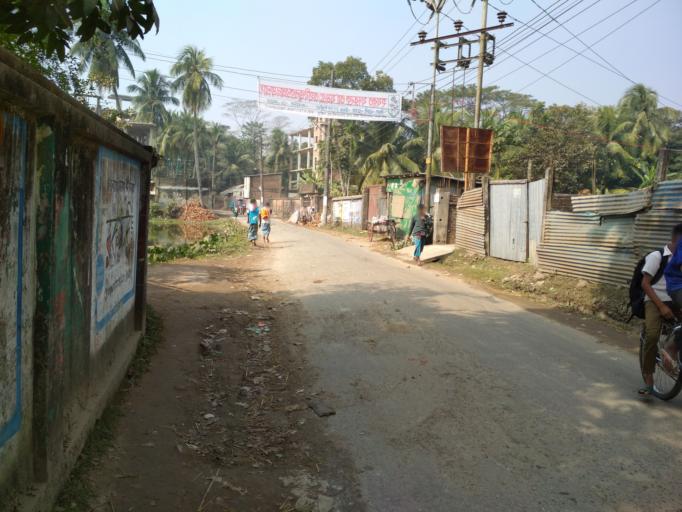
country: BD
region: Chittagong
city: Lakshmipur
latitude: 22.9346
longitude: 90.8257
